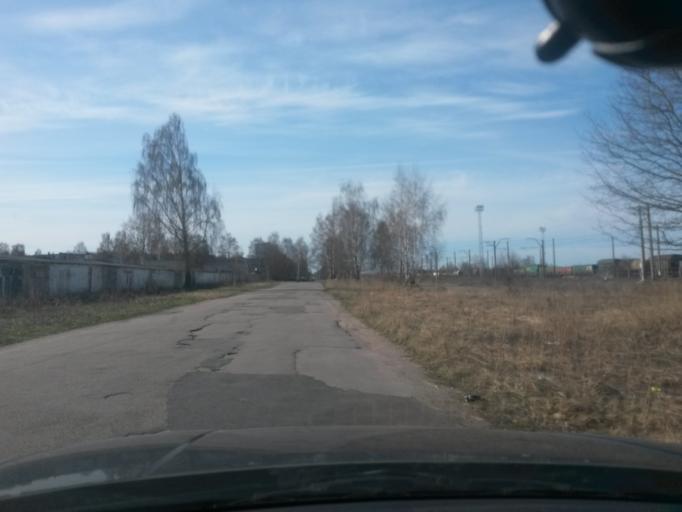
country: LV
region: Kekava
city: Kekava
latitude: 56.8988
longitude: 24.2215
